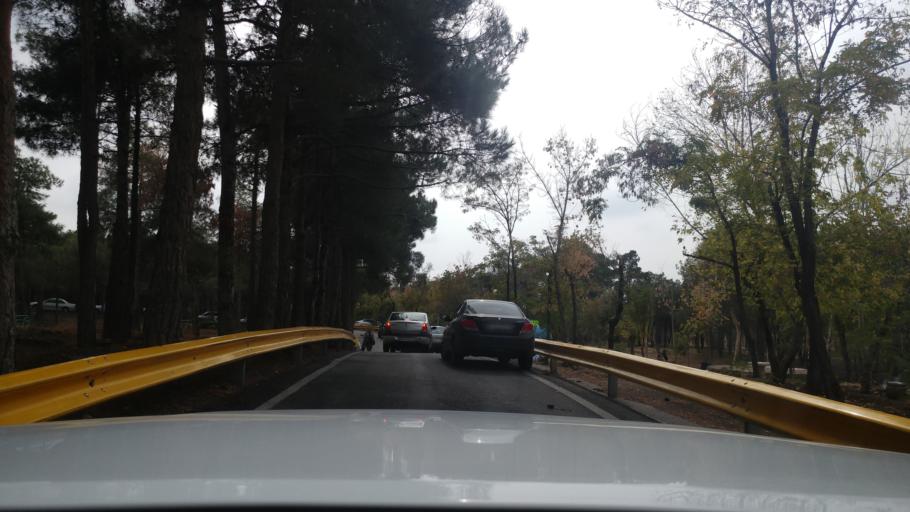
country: IR
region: Tehran
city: Shahr-e Qods
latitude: 35.7254
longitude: 51.2227
